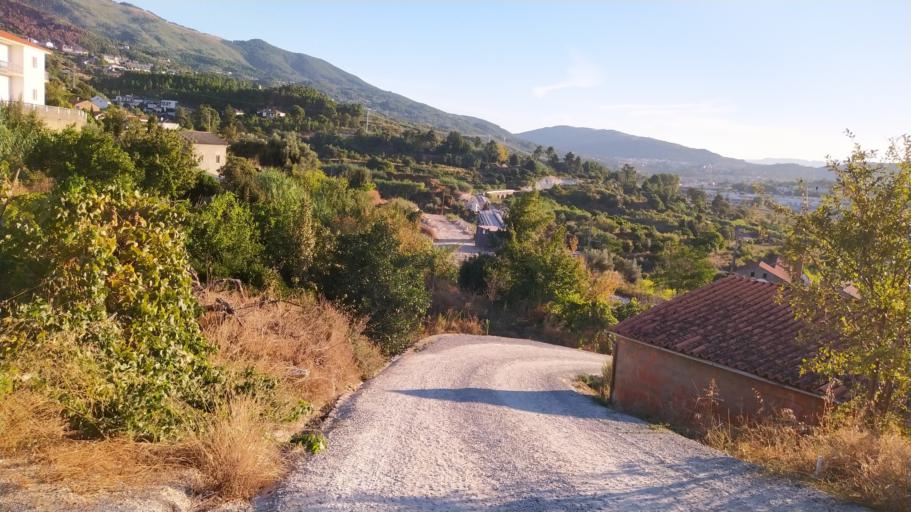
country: PT
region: Castelo Branco
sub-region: Covilha
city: Covilha
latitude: 40.2819
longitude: -7.4965
